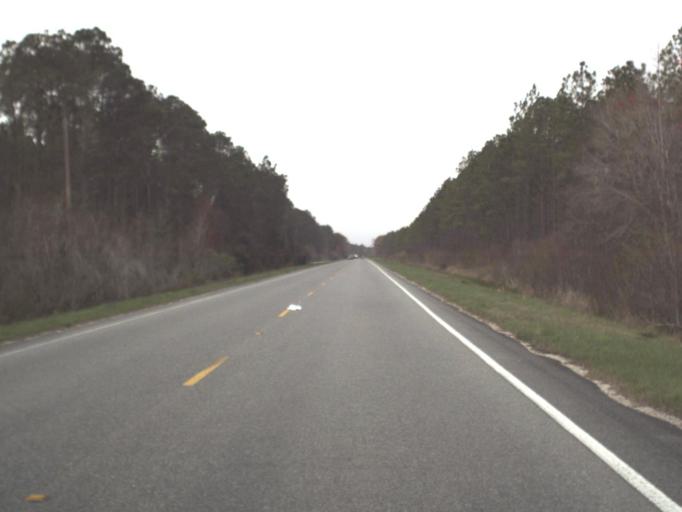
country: US
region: Florida
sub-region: Leon County
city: Woodville
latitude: 30.1924
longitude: -84.0999
